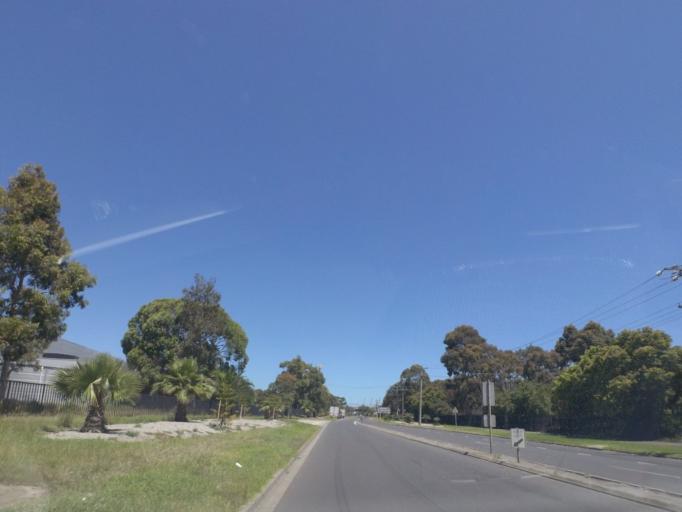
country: AU
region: Victoria
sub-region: Maribyrnong
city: Yarraville
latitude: -37.8274
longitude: 144.9118
